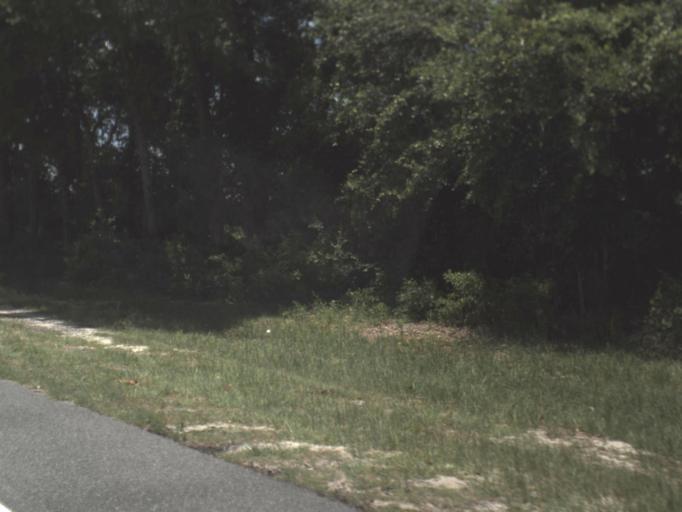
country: US
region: Florida
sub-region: Dixie County
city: Cross City
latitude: 29.8642
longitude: -82.9596
